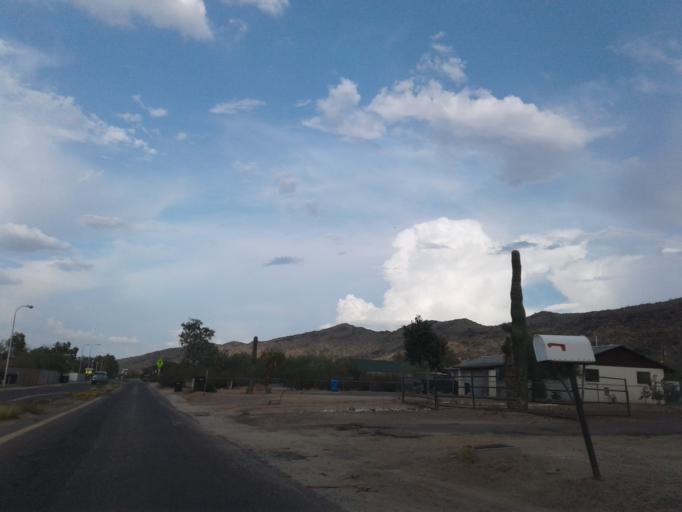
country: US
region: Arizona
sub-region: Maricopa County
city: Guadalupe
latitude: 33.3705
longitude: -112.0287
